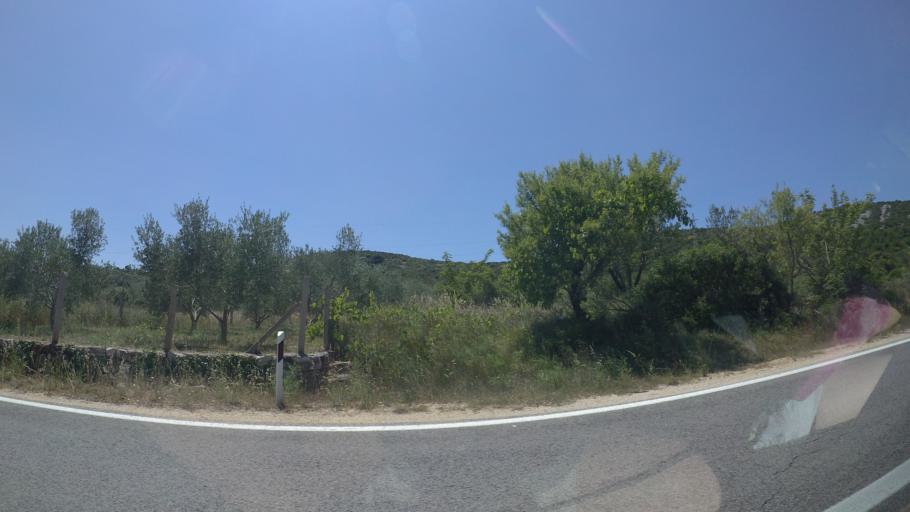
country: HR
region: Sibensko-Kniniska
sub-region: Grad Sibenik
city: Pirovac
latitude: 43.7984
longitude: 15.6768
